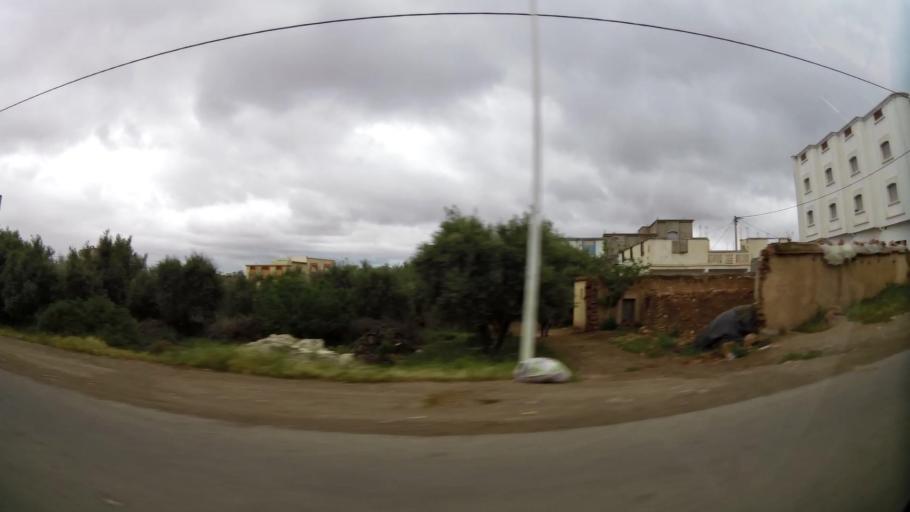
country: MA
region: Oriental
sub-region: Nador
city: Midar
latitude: 35.0560
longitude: -3.4635
